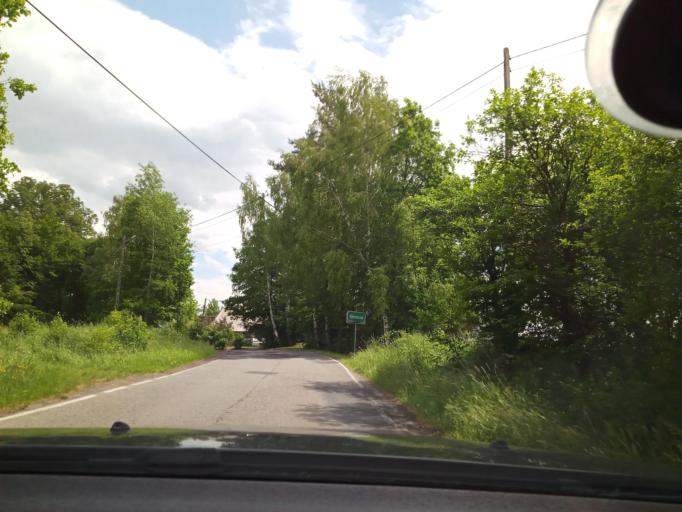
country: PL
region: Lesser Poland Voivodeship
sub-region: Powiat bochenski
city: Lapanow
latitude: 49.8542
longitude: 20.2524
